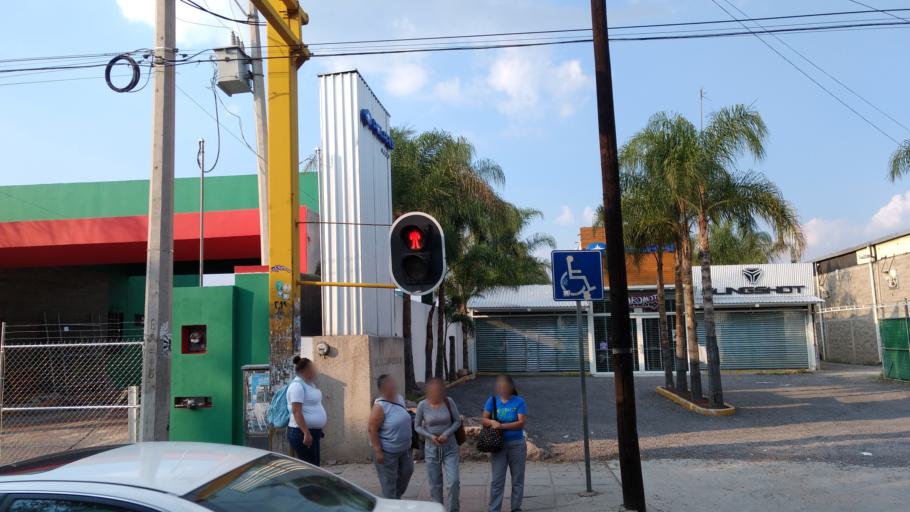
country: MX
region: Guanajuato
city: Leon
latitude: 21.1474
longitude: -101.6835
